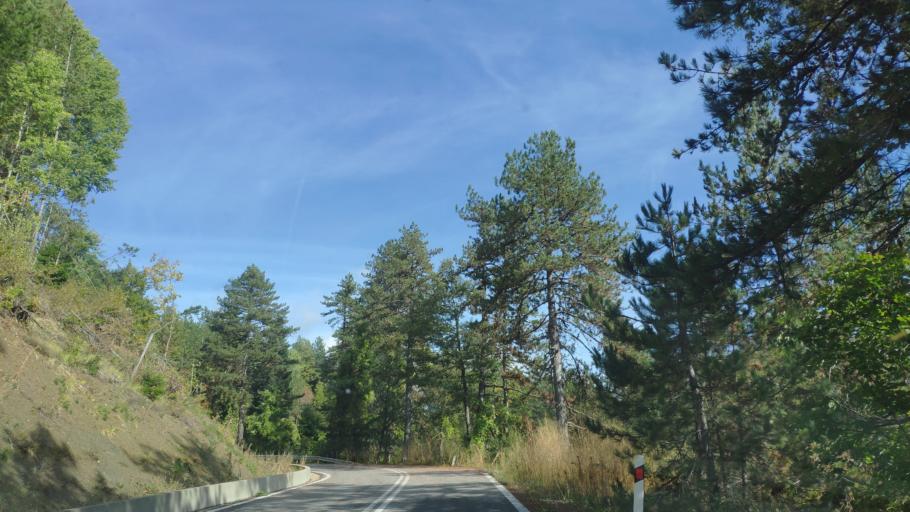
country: AL
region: Korce
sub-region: Rrethi i Devollit
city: Miras
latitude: 40.3732
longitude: 20.9231
